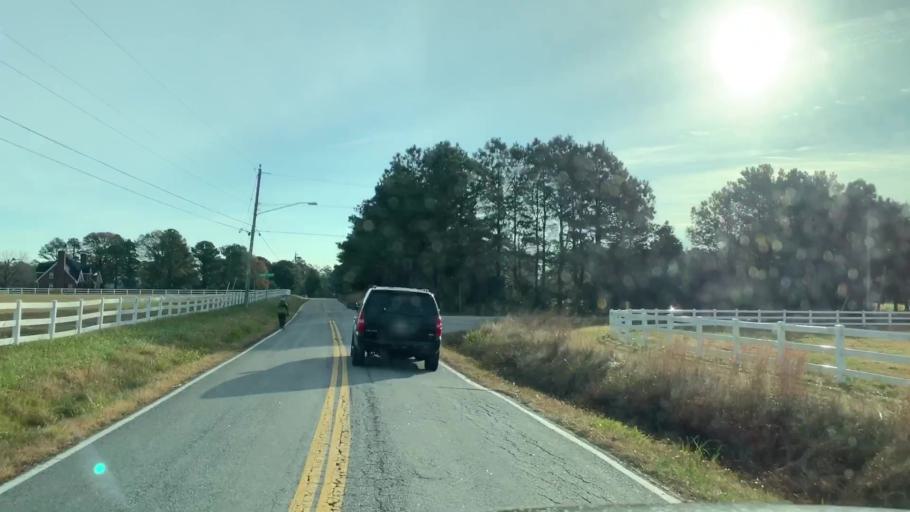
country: US
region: Virginia
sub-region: City of Virginia Beach
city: Virginia Beach
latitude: 36.6868
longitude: -75.9995
